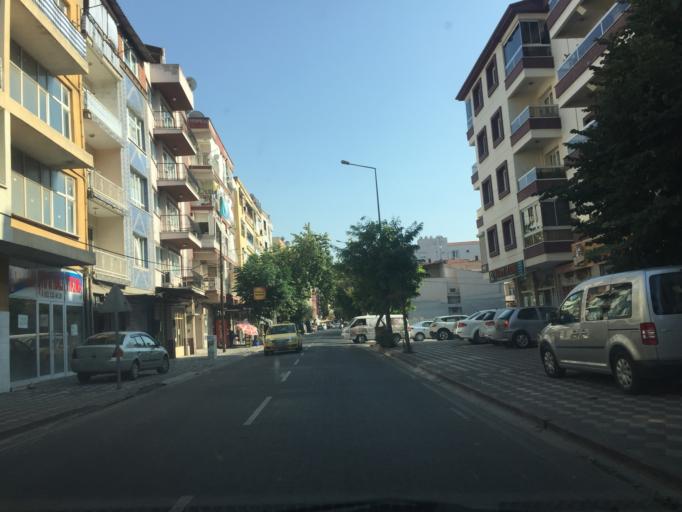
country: TR
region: Manisa
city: Akhisar
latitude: 38.9159
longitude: 27.8419
